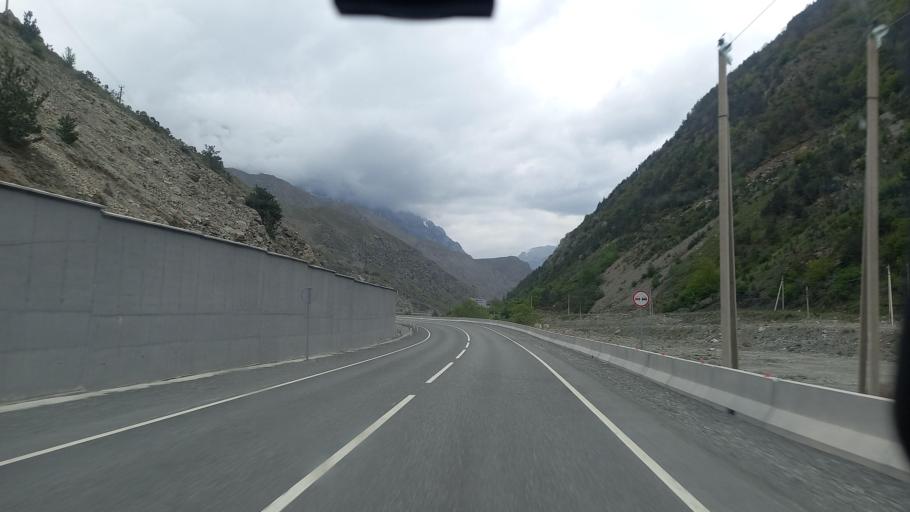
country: RU
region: North Ossetia
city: Mizur
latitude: 42.8405
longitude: 44.0317
